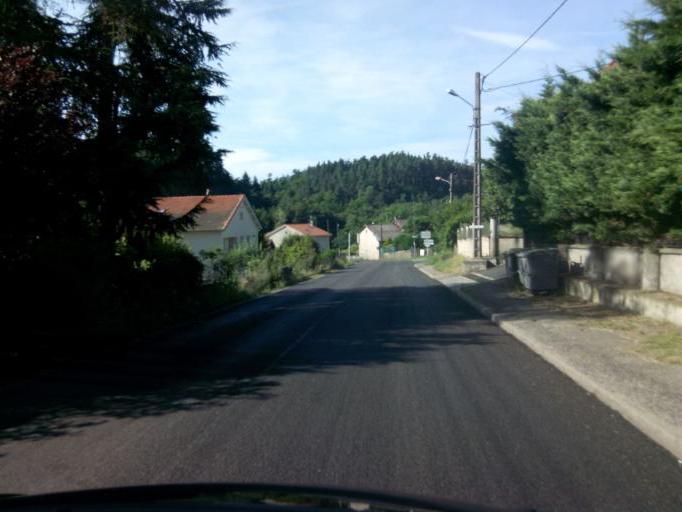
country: FR
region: Auvergne
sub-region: Departement de la Haute-Loire
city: Bas-en-Basset
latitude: 45.2875
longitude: 4.1140
